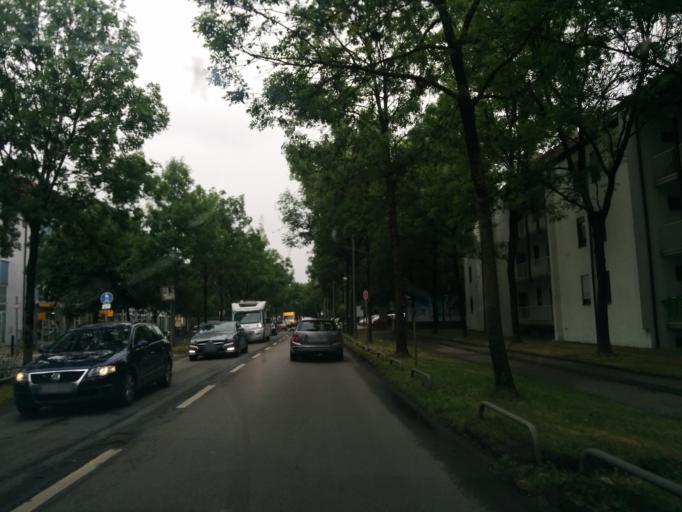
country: DE
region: Bavaria
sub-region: Upper Bavaria
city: Karlsfeld
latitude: 48.1876
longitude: 11.5035
